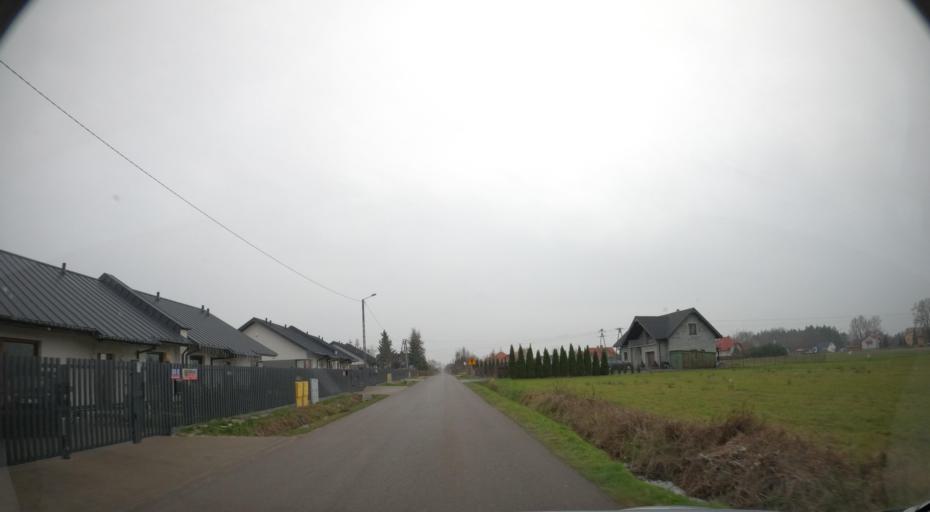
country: PL
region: Masovian Voivodeship
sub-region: Powiat radomski
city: Jastrzebia
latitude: 51.4243
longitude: 21.2379
